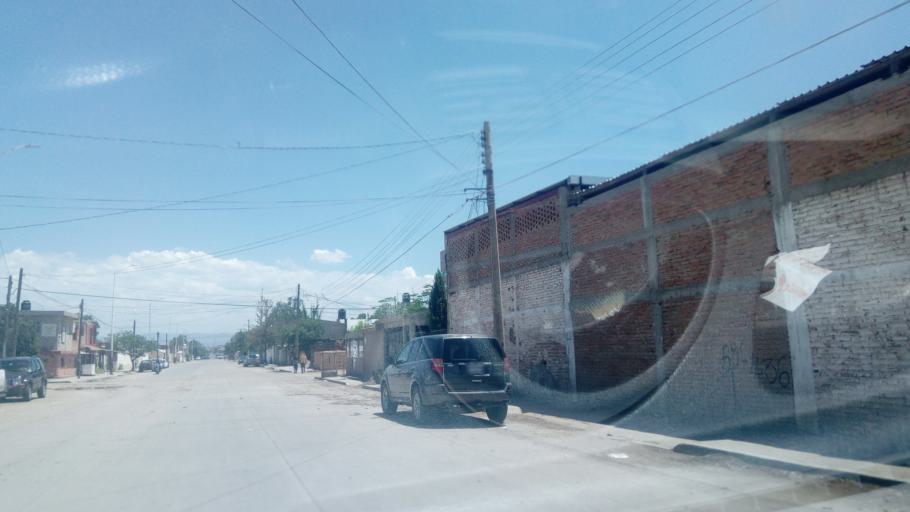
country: MX
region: Durango
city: Victoria de Durango
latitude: 24.0150
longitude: -104.6288
